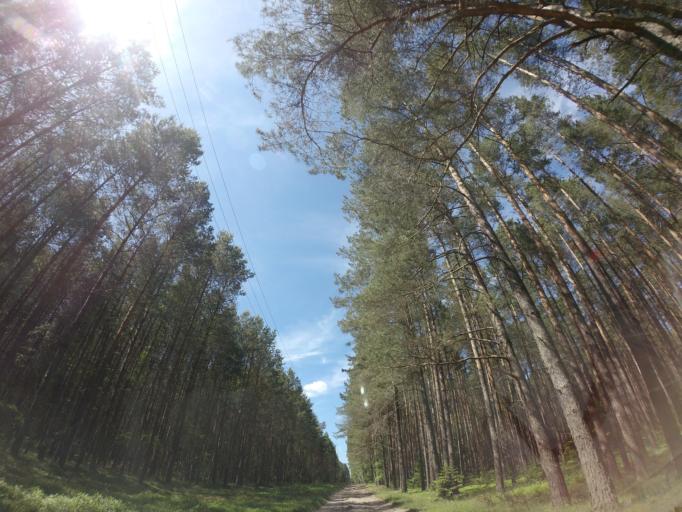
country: PL
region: West Pomeranian Voivodeship
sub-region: Powiat choszczenski
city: Drawno
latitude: 53.1196
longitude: 15.8070
